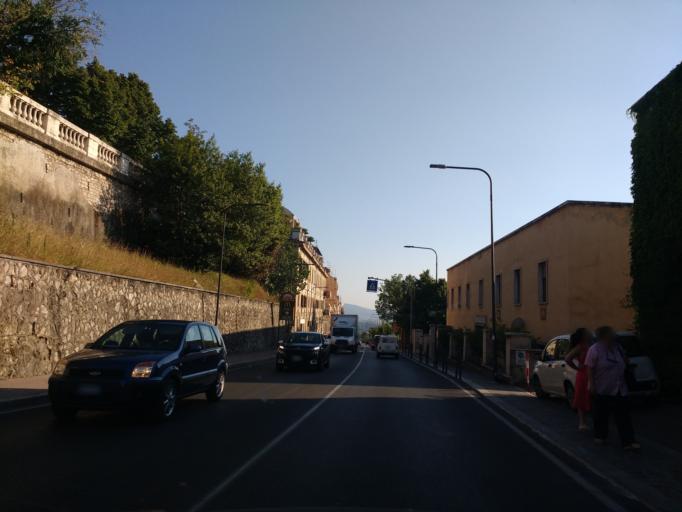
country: IT
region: Latium
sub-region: Citta metropolitana di Roma Capitale
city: Tivoli
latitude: 41.9585
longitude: 12.7938
